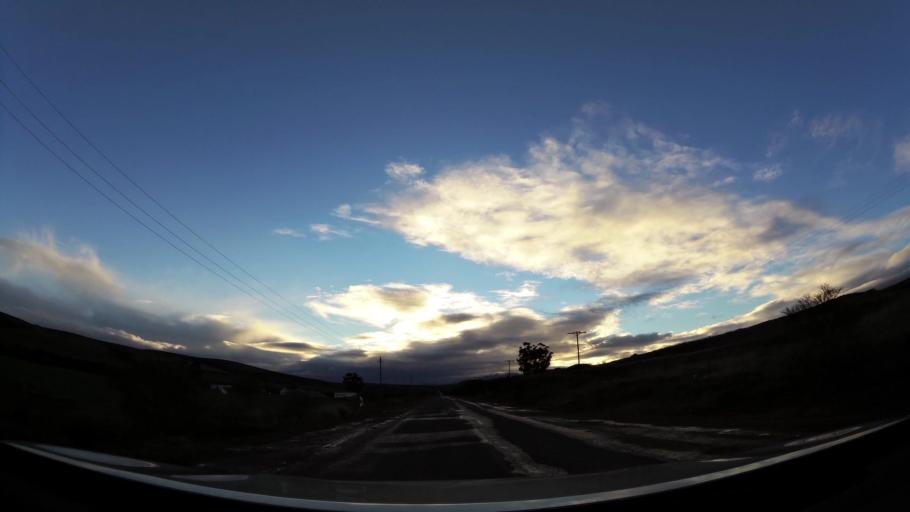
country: ZA
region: Western Cape
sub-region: Eden District Municipality
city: Riversdale
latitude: -34.0619
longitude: 20.8820
